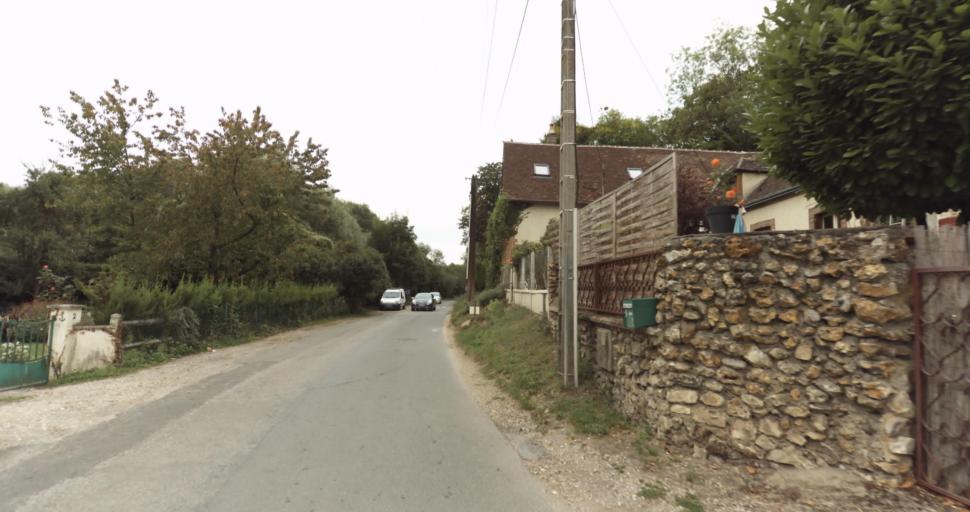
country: FR
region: Centre
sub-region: Departement d'Eure-et-Loir
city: Vert-en-Drouais
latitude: 48.7680
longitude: 1.3003
